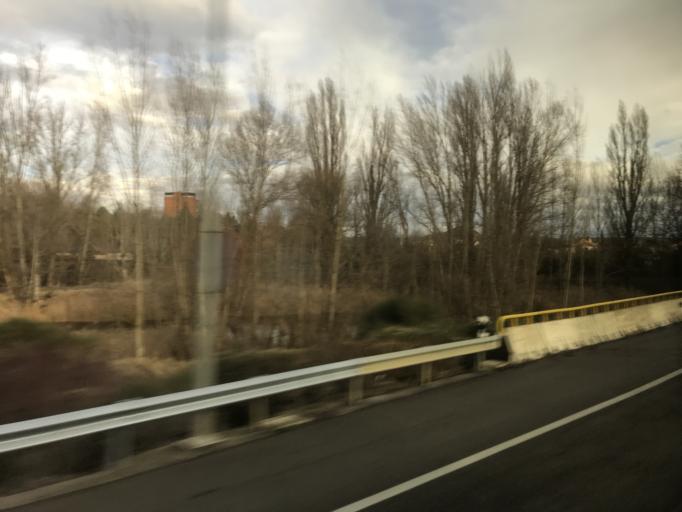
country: ES
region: Castille and Leon
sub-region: Provincia de Palencia
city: Grijota
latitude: 42.0353
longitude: -4.5584
